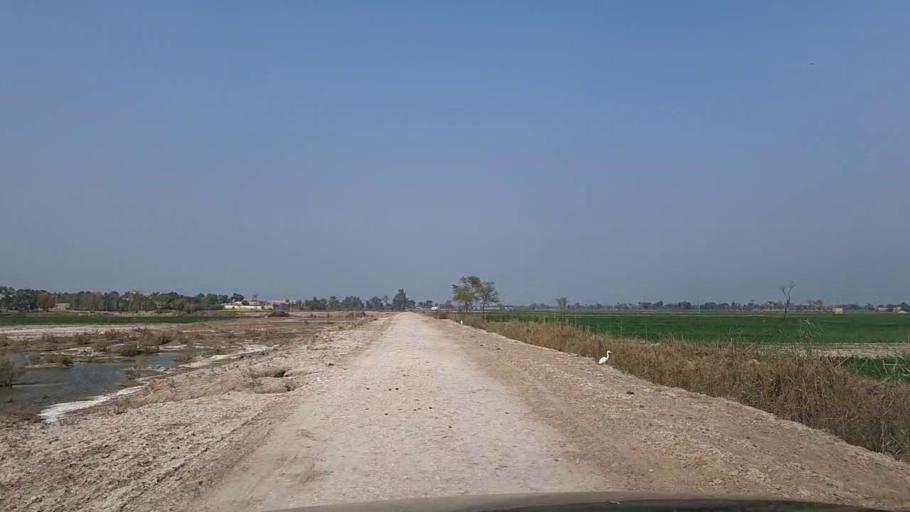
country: PK
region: Sindh
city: Daur
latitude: 26.3891
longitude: 68.4236
